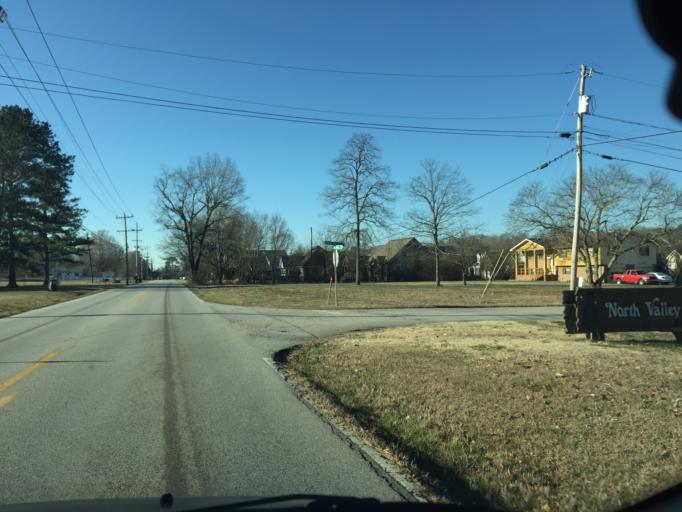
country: US
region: Tennessee
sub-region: Hamilton County
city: Collegedale
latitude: 35.0329
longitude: -85.0805
